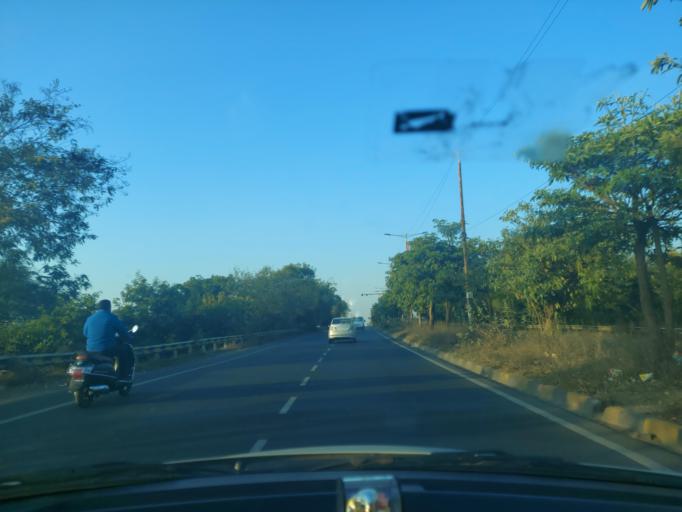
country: IN
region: Madhya Pradesh
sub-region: Ujjain
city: Ujjain
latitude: 23.1270
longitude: 75.7955
